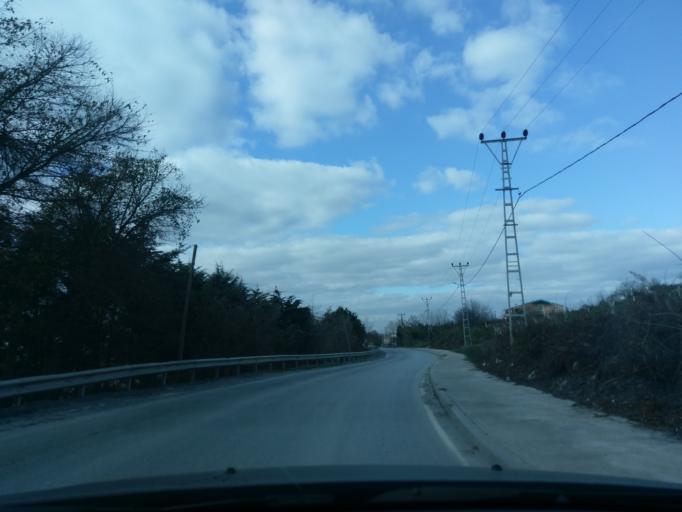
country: TR
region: Istanbul
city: Durusu
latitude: 41.2626
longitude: 28.6788
